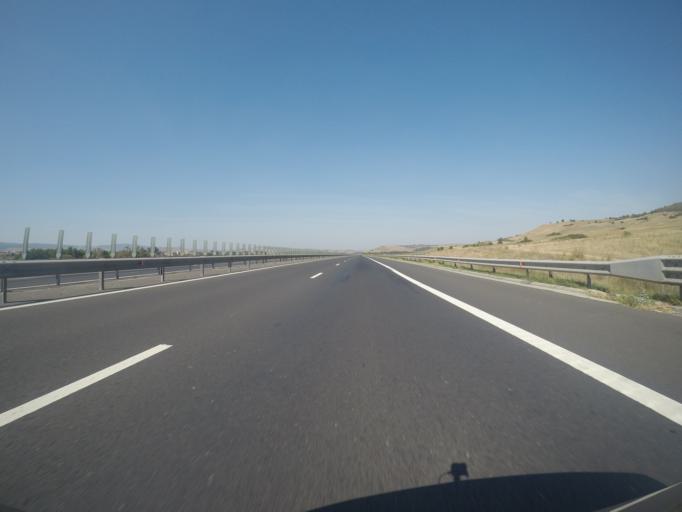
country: RO
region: Sibiu
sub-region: Oras Miercurea Sibiului
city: Miercurea Sibiului
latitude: 45.8947
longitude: 23.8170
